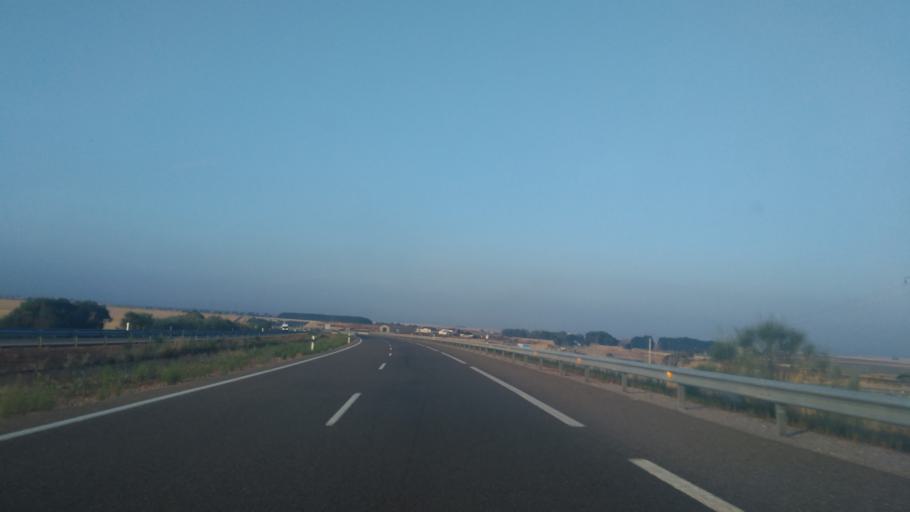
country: ES
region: Castille and Leon
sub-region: Provincia de Salamanca
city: Galindo y Perahuy
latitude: 40.9156
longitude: -5.8602
